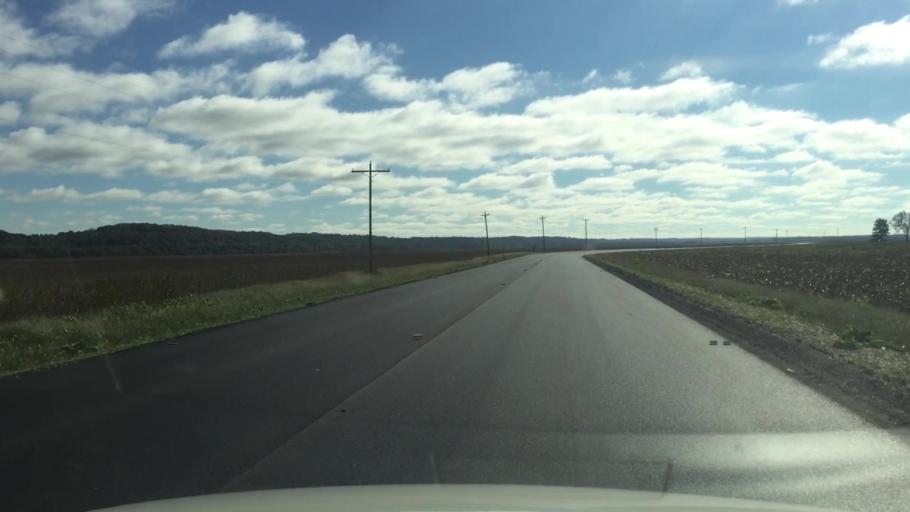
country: US
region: Missouri
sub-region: Howard County
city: New Franklin
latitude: 39.0003
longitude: -92.6772
